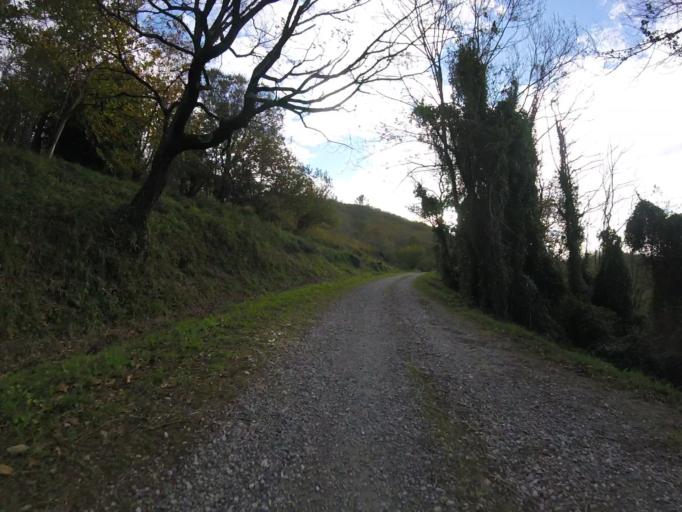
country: ES
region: Basque Country
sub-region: Provincia de Guipuzcoa
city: Errenteria
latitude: 43.2990
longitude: -1.9177
